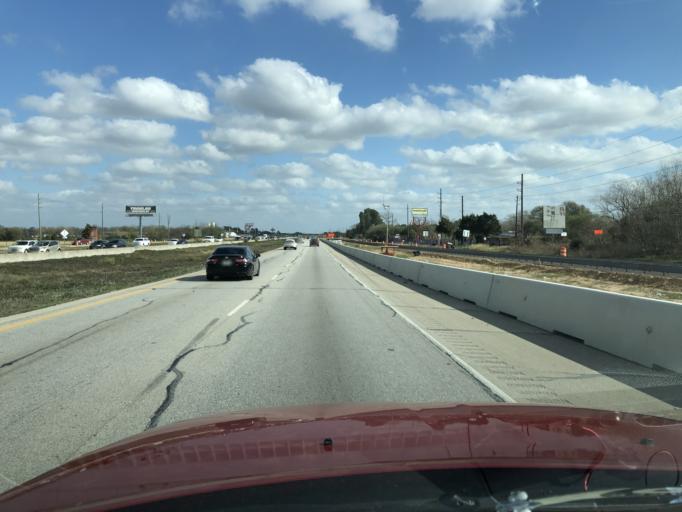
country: US
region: Texas
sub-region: Austin County
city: Sealy
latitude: 29.7755
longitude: -96.1220
